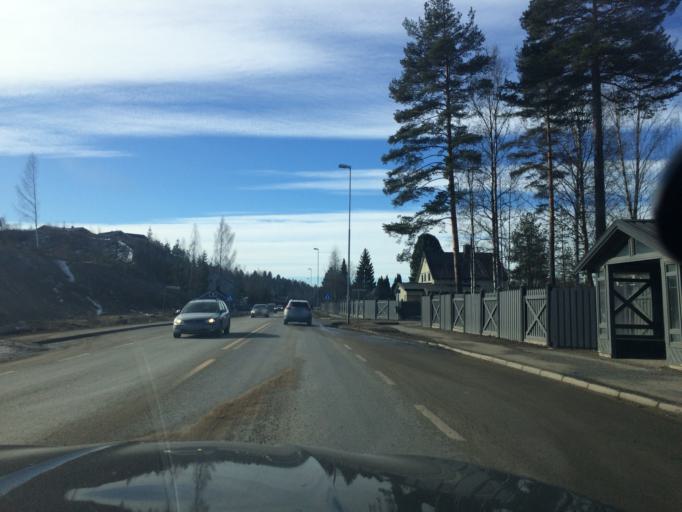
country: NO
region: Hedmark
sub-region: Elverum
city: Elverum
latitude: 60.8923
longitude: 11.5746
